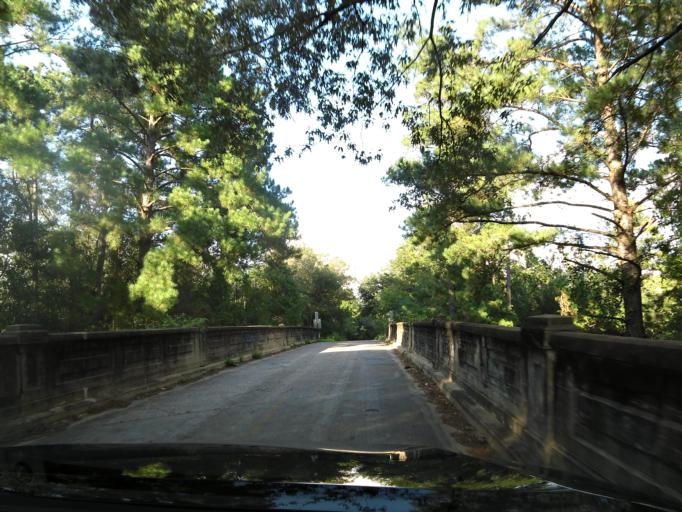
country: US
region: Georgia
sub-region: Lowndes County
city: Remerton
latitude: 30.7978
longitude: -83.3871
